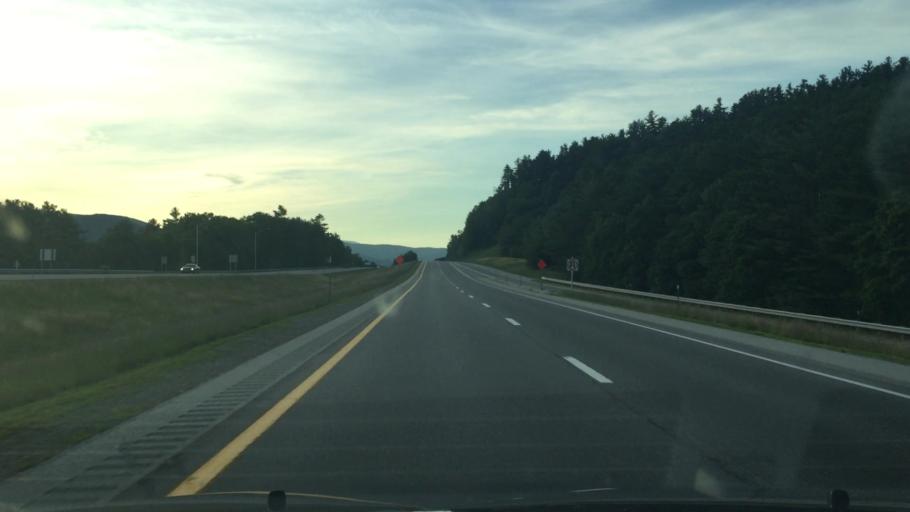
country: US
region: New Hampshire
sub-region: Grafton County
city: Thornton
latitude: 43.8522
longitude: -71.6468
